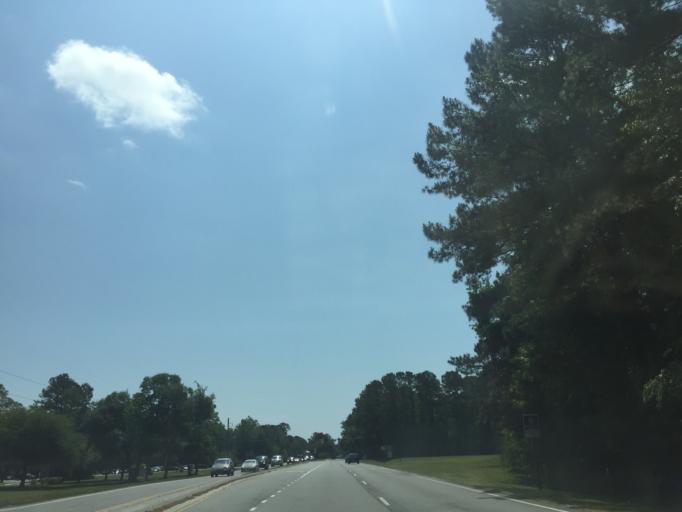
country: US
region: Georgia
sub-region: Chatham County
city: Skidaway Island
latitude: 31.9415
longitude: -81.0583
